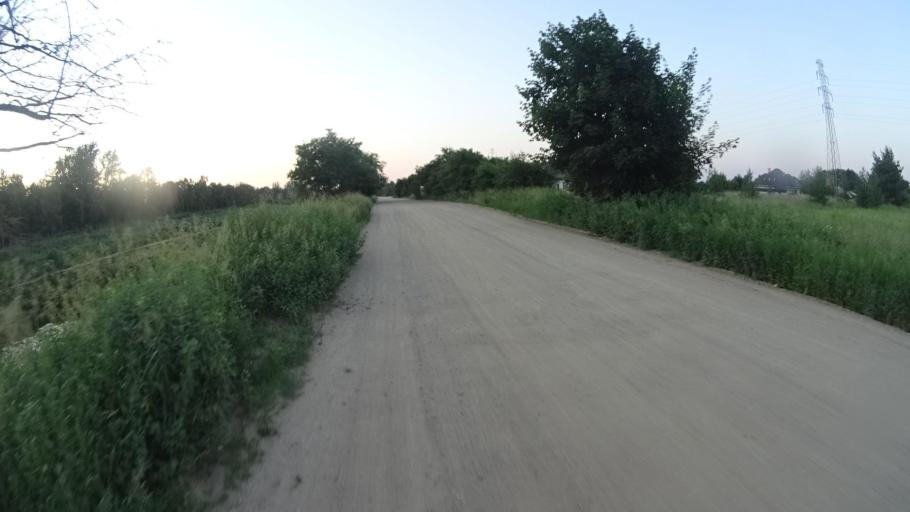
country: PL
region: Masovian Voivodeship
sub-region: Powiat legionowski
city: Stanislawow Pierwszy
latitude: 52.3430
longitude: 21.0337
